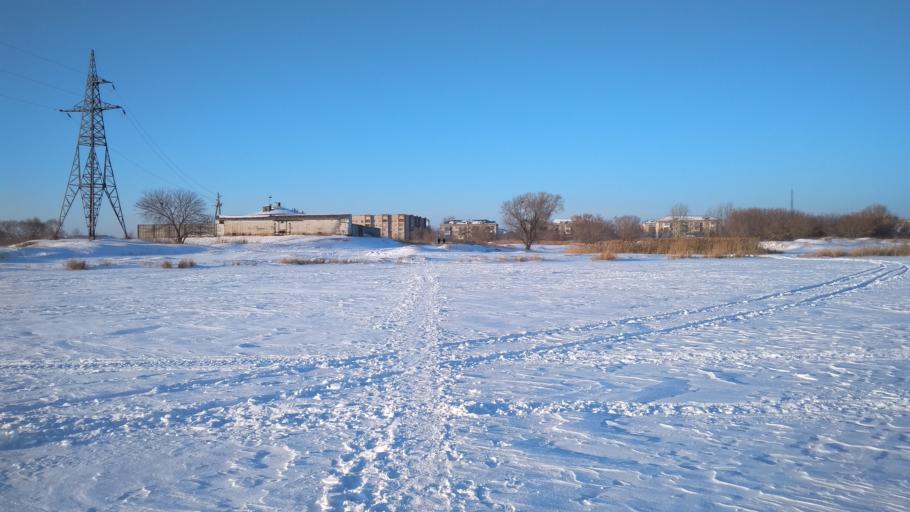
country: RU
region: Chelyabinsk
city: Troitsk
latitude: 54.0809
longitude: 61.5793
